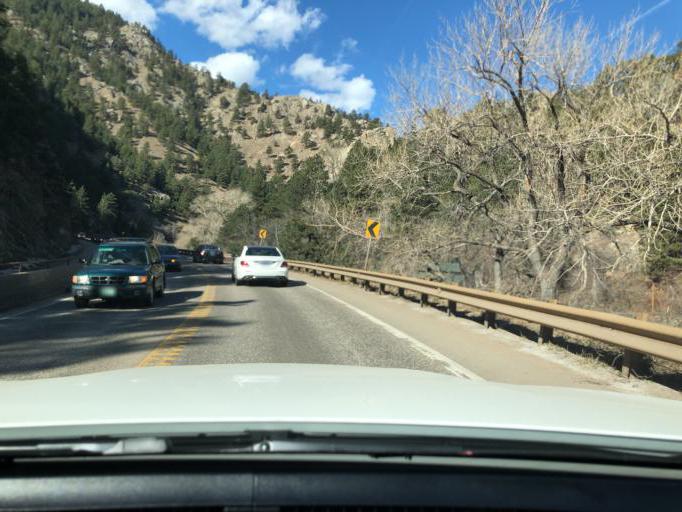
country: US
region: Colorado
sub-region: Boulder County
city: Boulder
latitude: 40.0122
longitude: -105.3058
